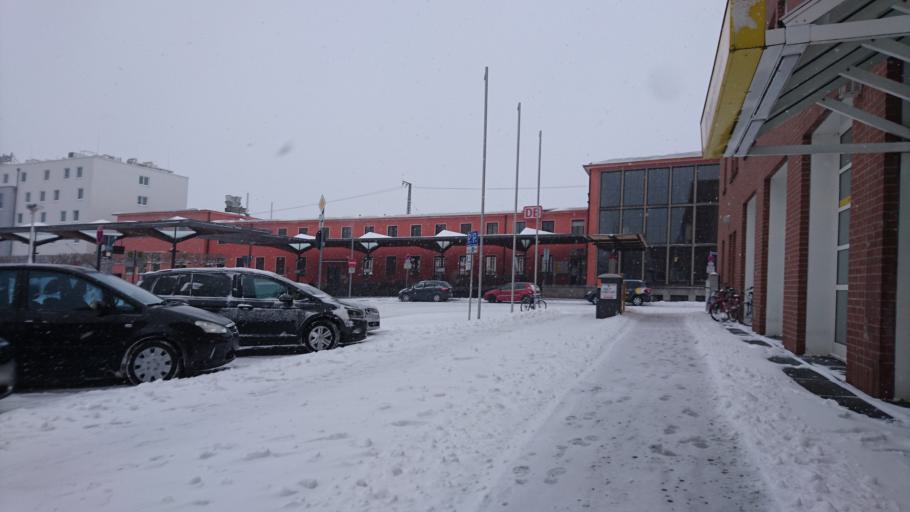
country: DE
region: Bavaria
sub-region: Upper Bavaria
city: Ingolstadt
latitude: 48.7443
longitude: 11.4359
